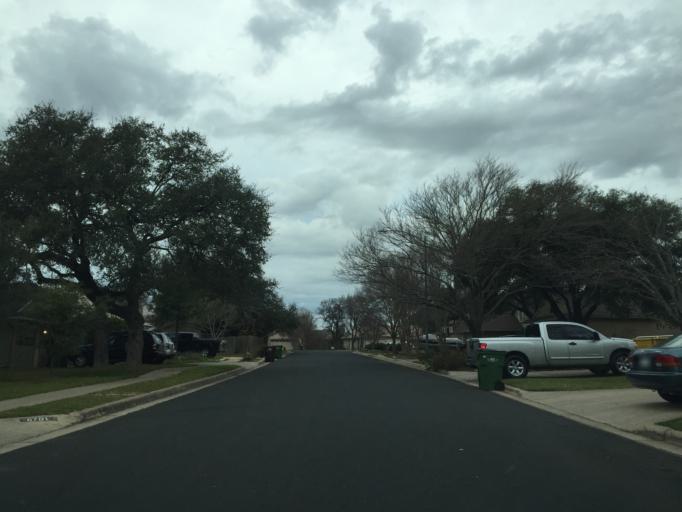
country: US
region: Texas
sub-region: Williamson County
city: Jollyville
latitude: 30.4481
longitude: -97.7462
